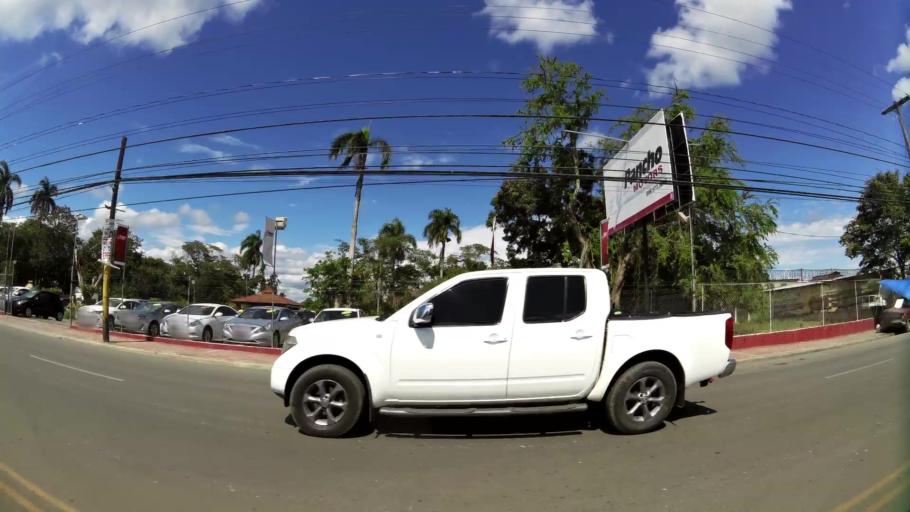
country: DO
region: La Vega
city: Concepcion de La Vega
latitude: 19.2350
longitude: -70.5318
